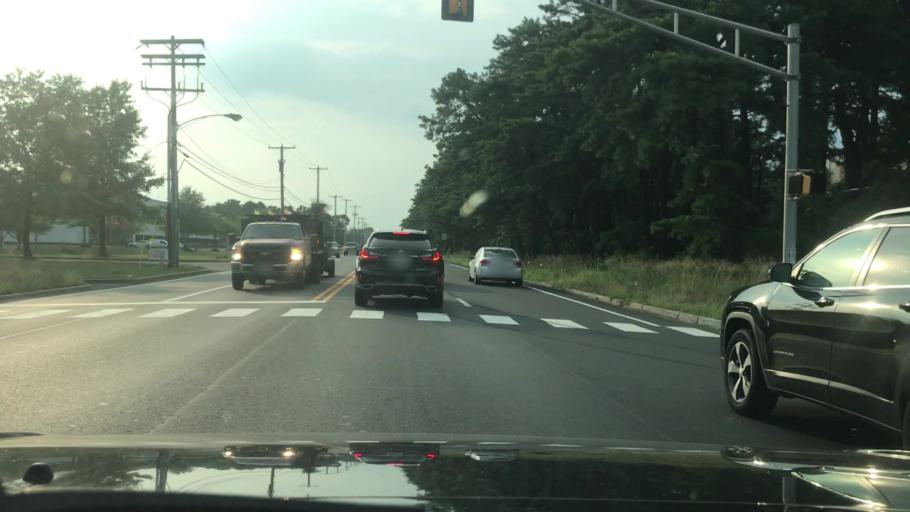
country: US
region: New Jersey
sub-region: Ocean County
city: Leisure Village
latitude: 40.0712
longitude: -74.1730
